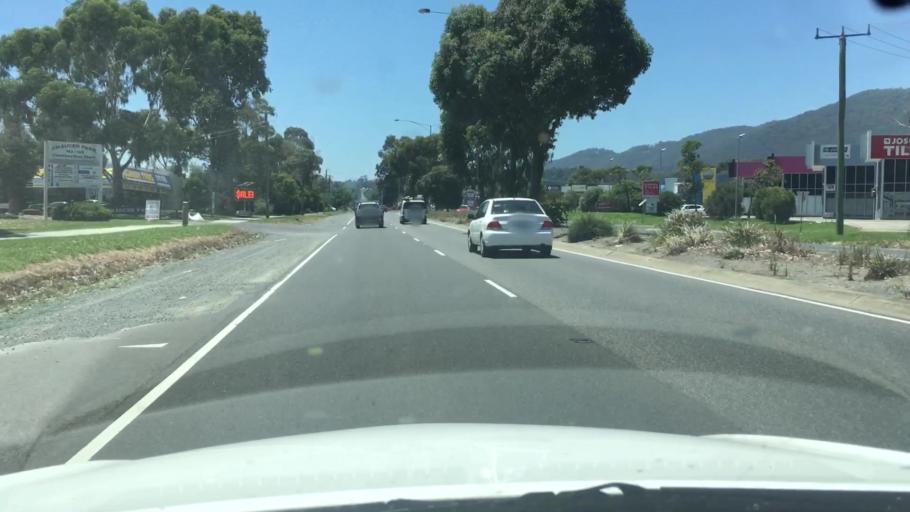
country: AU
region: Victoria
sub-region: Maroondah
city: Kilsyth South
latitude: -37.8198
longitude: 145.3104
